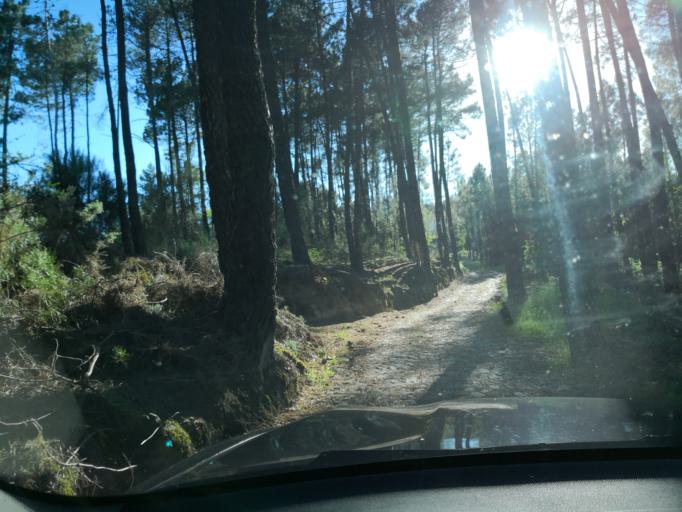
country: PT
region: Vila Real
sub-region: Vila Real
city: Vila Real
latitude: 41.3326
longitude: -7.7493
